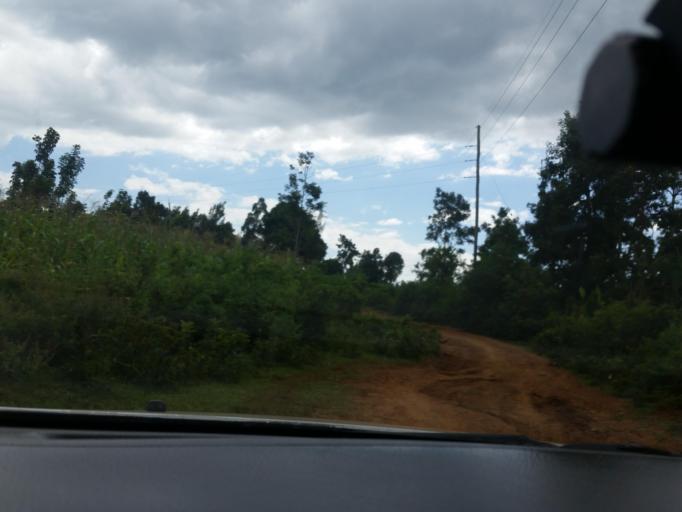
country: KE
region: Siaya
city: Yala
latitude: 0.1074
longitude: 34.4114
